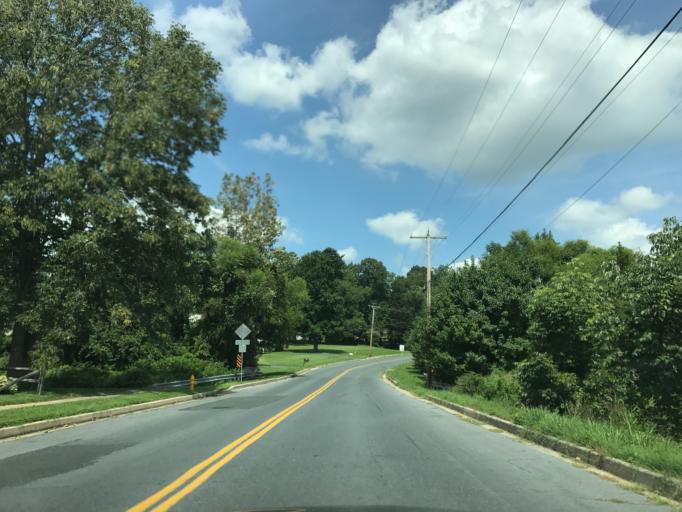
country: US
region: Maryland
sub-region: Harford County
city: Riverside
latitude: 39.4777
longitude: -76.2750
